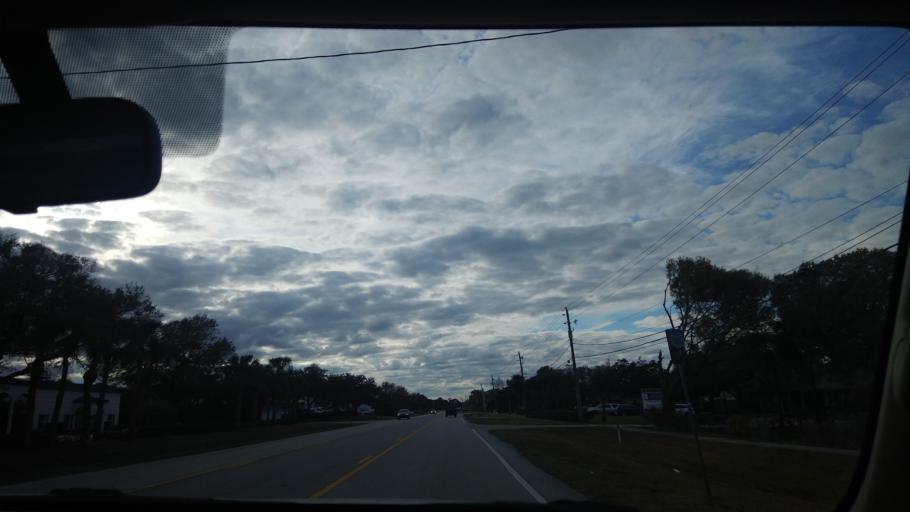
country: US
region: Florida
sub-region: Indian River County
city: Gifford
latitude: 27.6604
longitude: -80.3969
